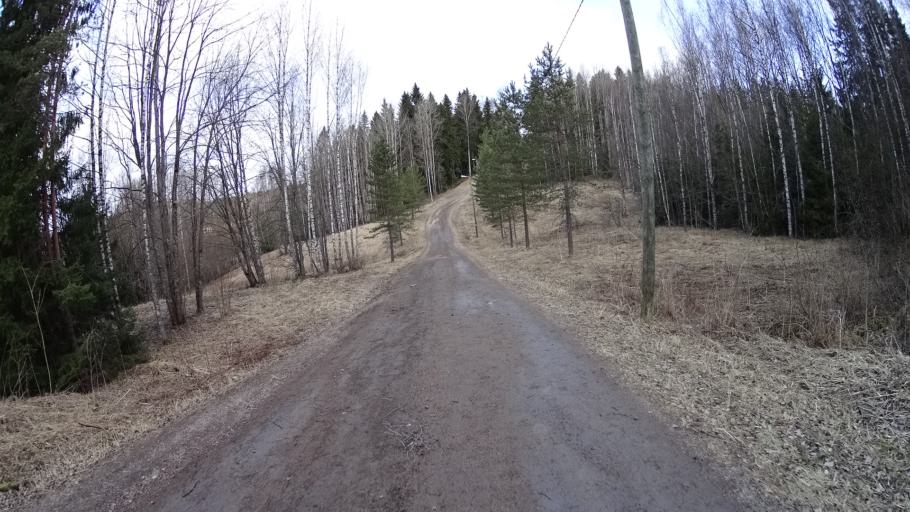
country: FI
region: Uusimaa
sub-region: Helsinki
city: Kilo
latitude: 60.2909
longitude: 24.8222
